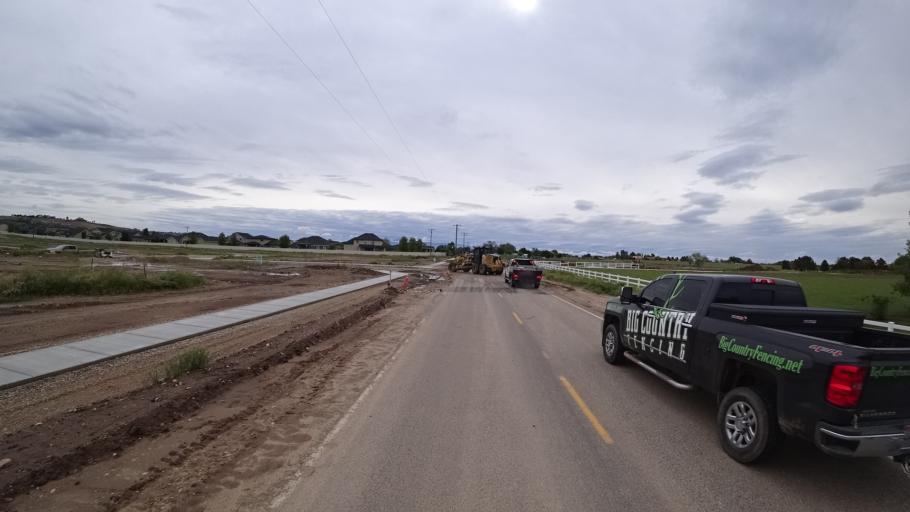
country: US
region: Idaho
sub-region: Ada County
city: Star
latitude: 43.7176
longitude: -116.4999
